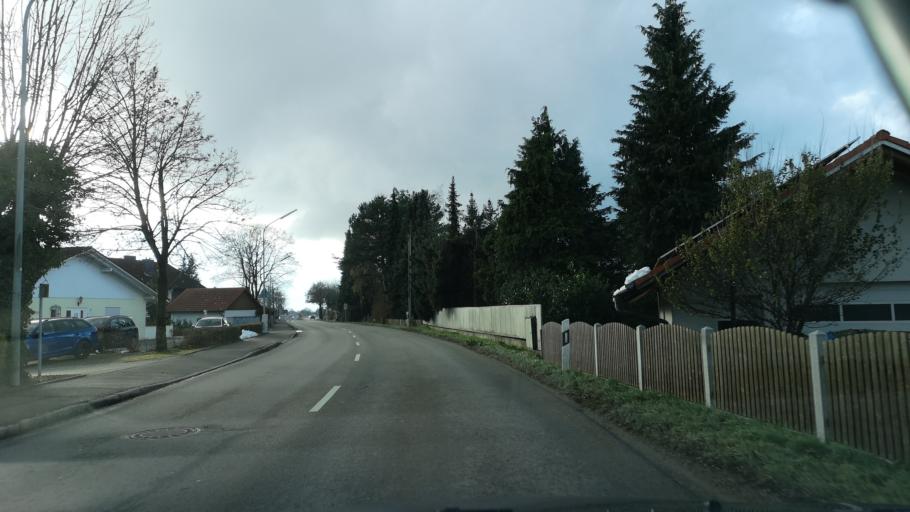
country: DE
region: Bavaria
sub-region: Upper Bavaria
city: Pliening
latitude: 48.1981
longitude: 11.7970
